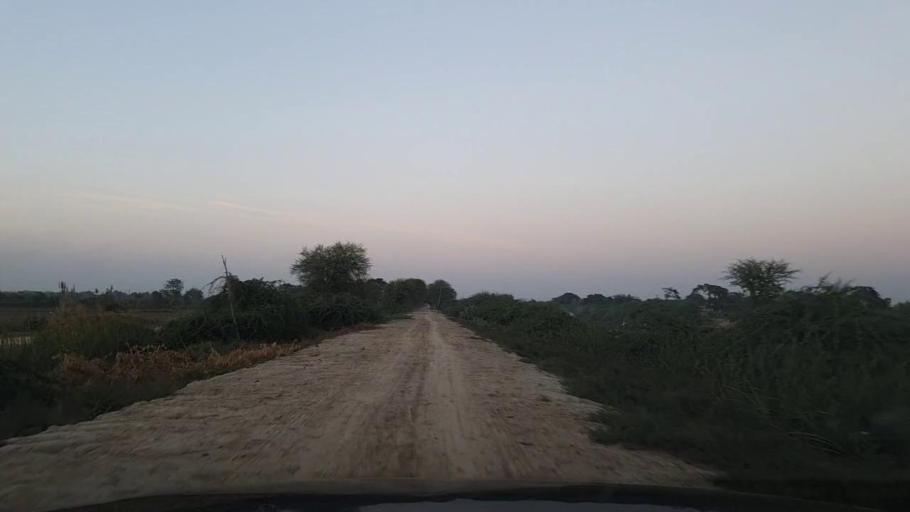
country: PK
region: Sindh
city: Thatta
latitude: 24.7440
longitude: 67.9574
